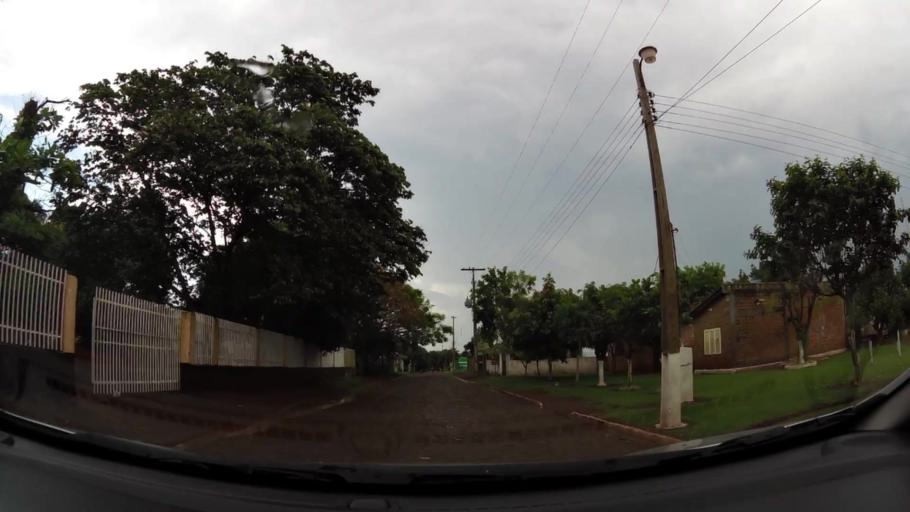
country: PY
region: Alto Parana
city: Presidente Franco
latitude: -25.5501
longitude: -54.6514
